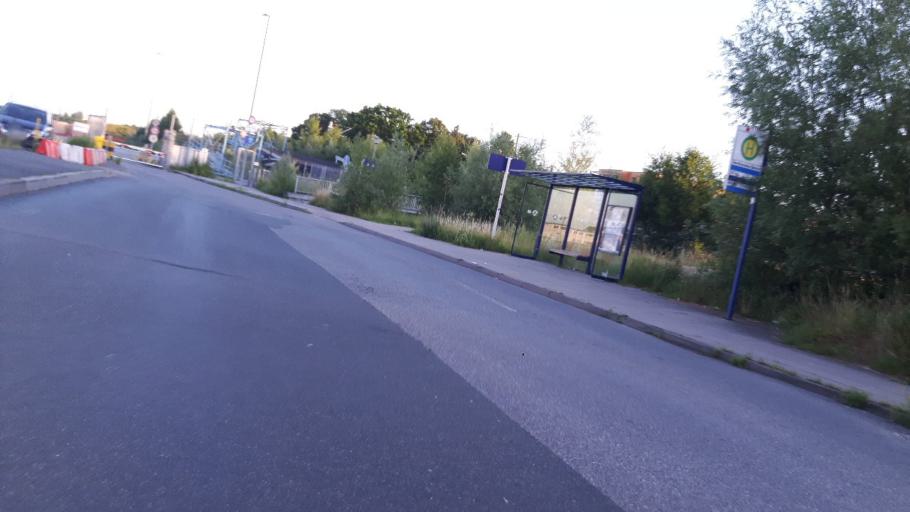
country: DE
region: Schleswig-Holstein
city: Travemuende
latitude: 53.9516
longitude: 10.8546
